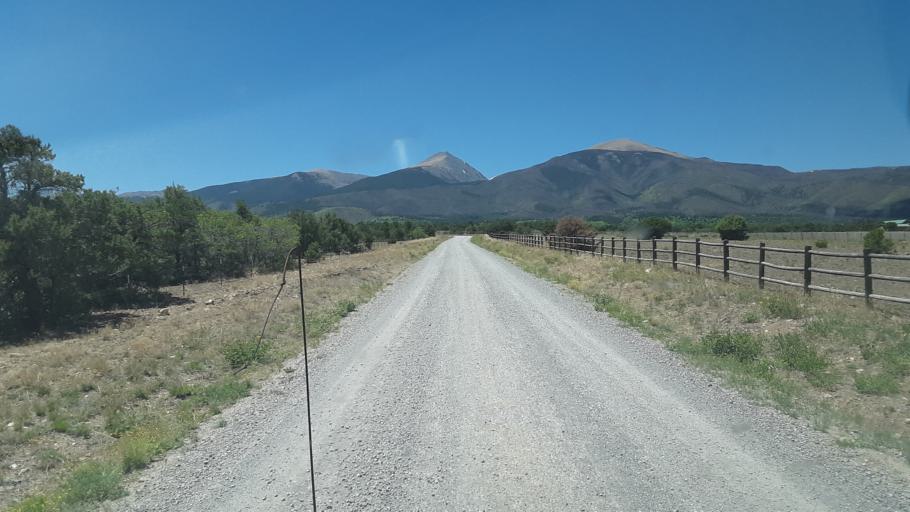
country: US
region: Colorado
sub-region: Custer County
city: Westcliffe
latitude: 38.3149
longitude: -105.6695
